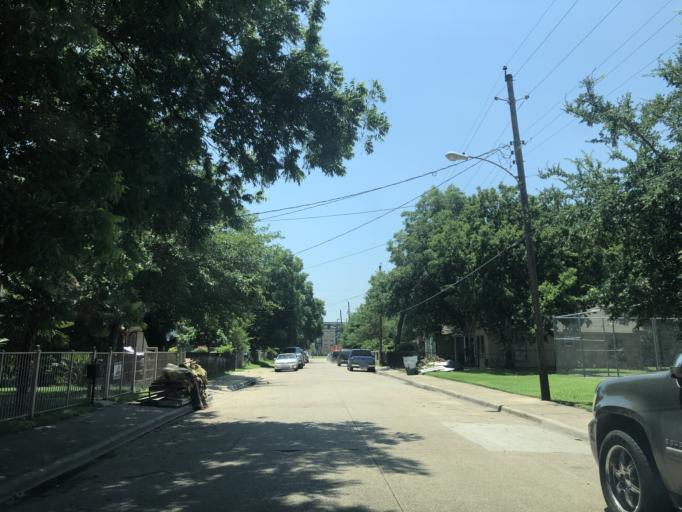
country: US
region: Texas
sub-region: Dallas County
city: Dallas
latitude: 32.7804
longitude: -96.8378
